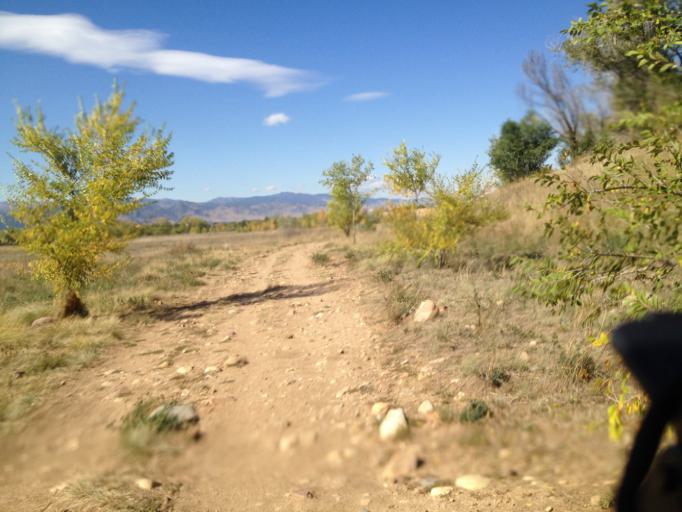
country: US
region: Colorado
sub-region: Boulder County
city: Boulder
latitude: 39.9788
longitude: -105.2290
